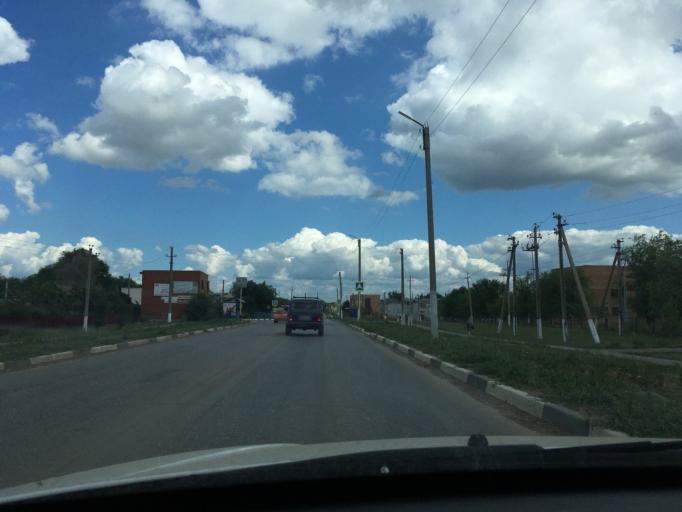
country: RU
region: Samara
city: Bezenchuk
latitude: 52.9907
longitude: 49.4363
